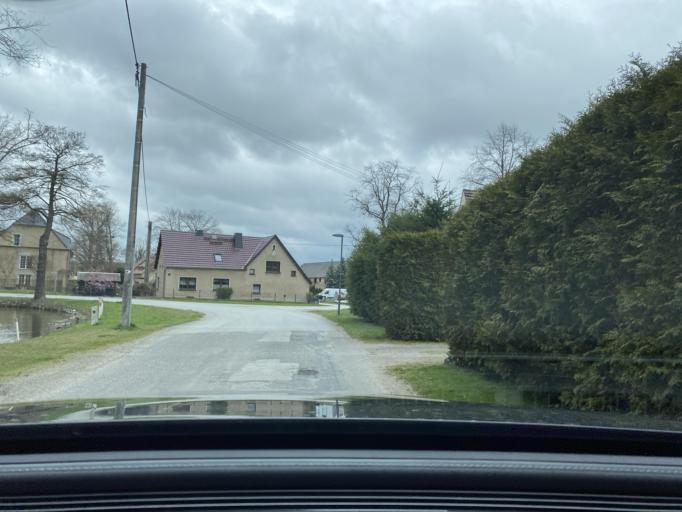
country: DE
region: Saxony
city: Neschwitz
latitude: 51.2498
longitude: 14.3479
